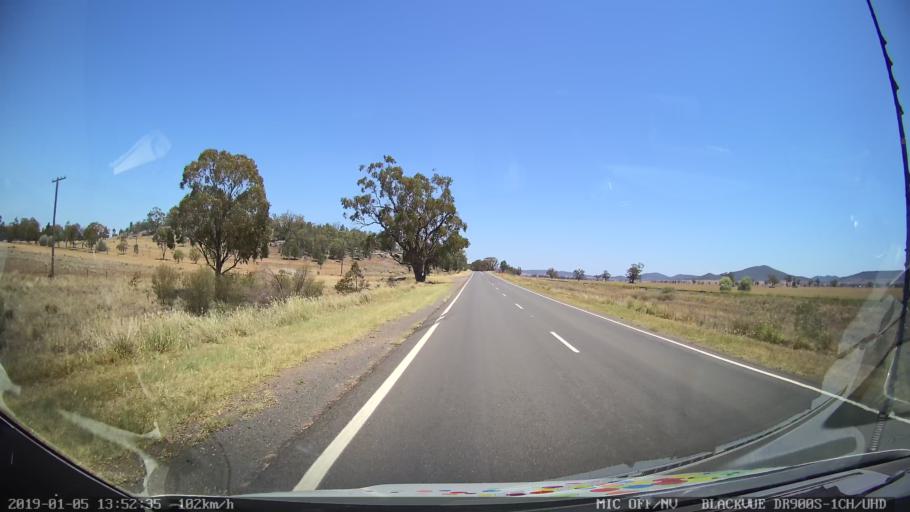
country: AU
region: New South Wales
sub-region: Gunnedah
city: Gunnedah
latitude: -31.0621
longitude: 150.2771
